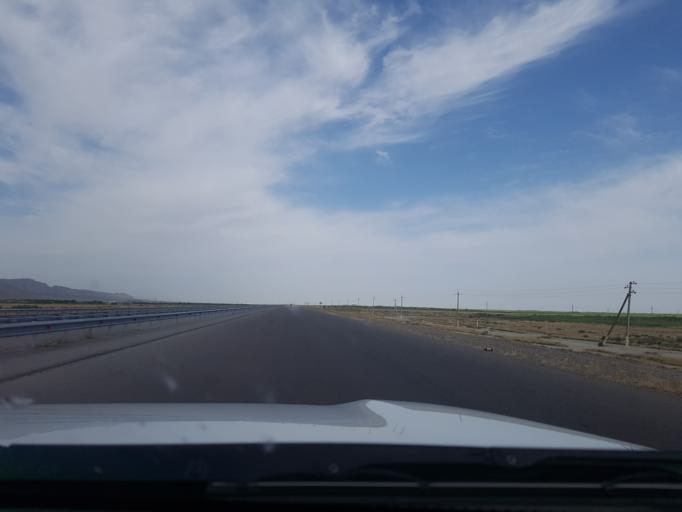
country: TM
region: Balkan
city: Serdar
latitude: 38.9205
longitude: 56.4704
